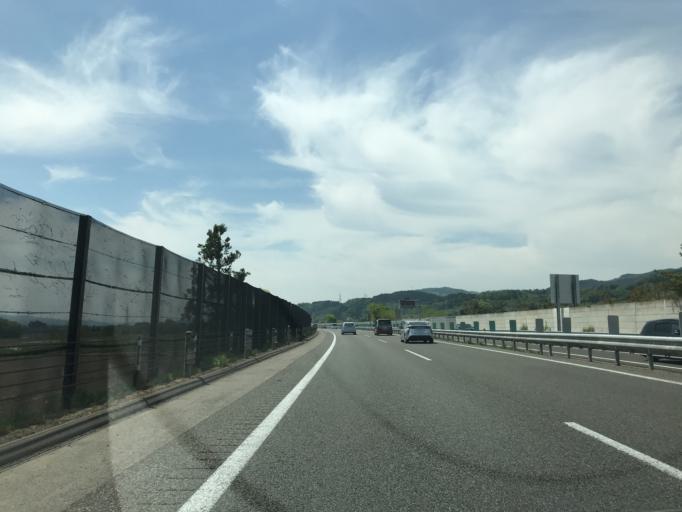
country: JP
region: Fukushima
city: Hobaramachi
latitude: 37.8775
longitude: 140.5269
